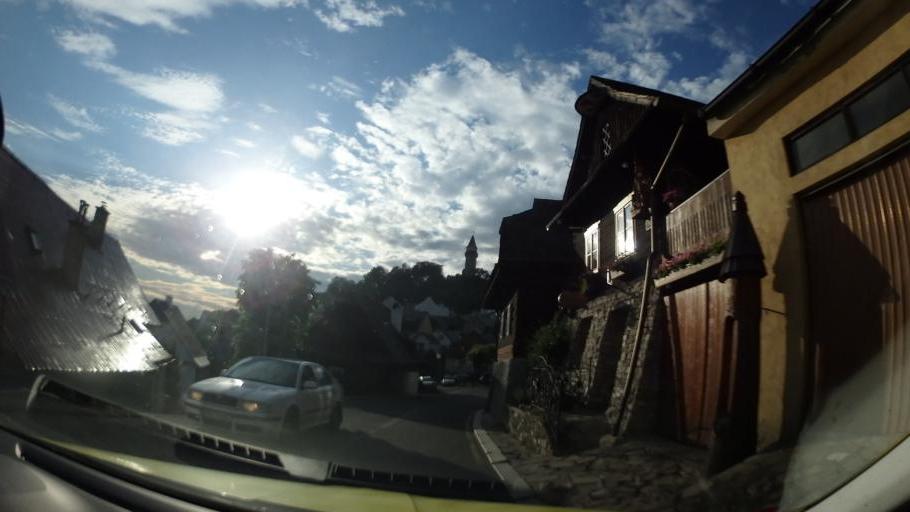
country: CZ
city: Stramberk
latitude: 49.5899
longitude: 18.1199
